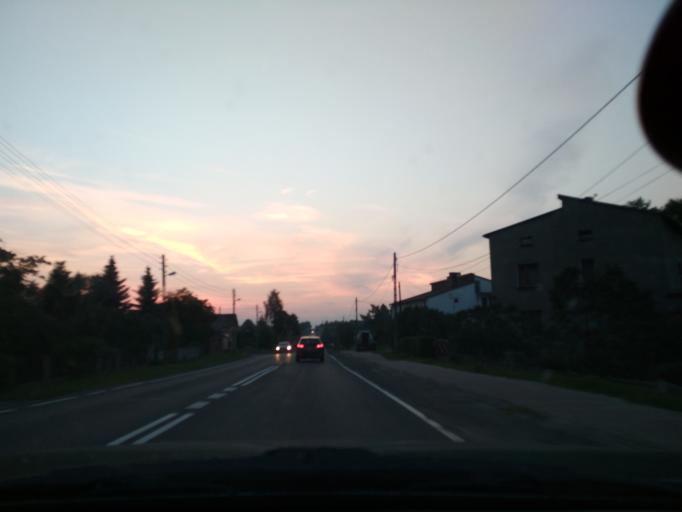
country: PL
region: Silesian Voivodeship
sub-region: Powiat zawiercianski
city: Ogrodzieniec
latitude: 50.4667
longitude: 19.4884
